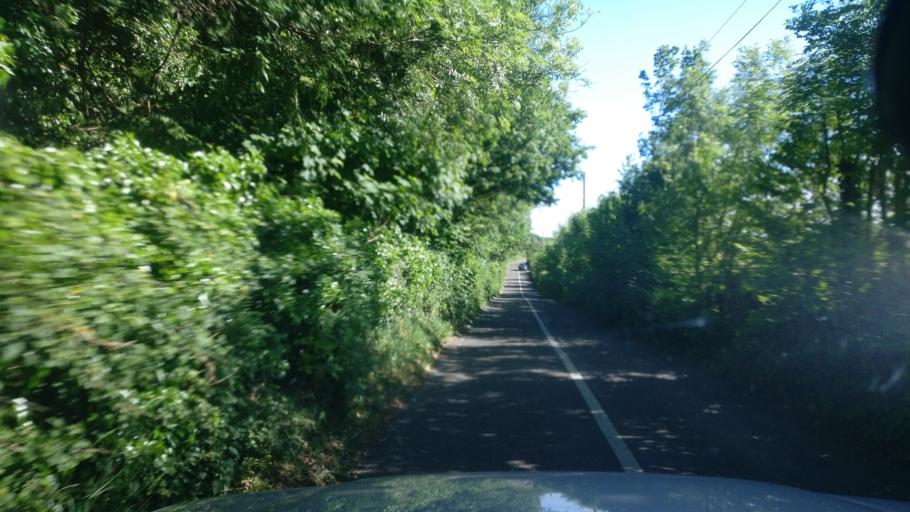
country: IE
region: Connaught
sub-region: County Galway
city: Loughrea
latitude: 53.2368
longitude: -8.6230
